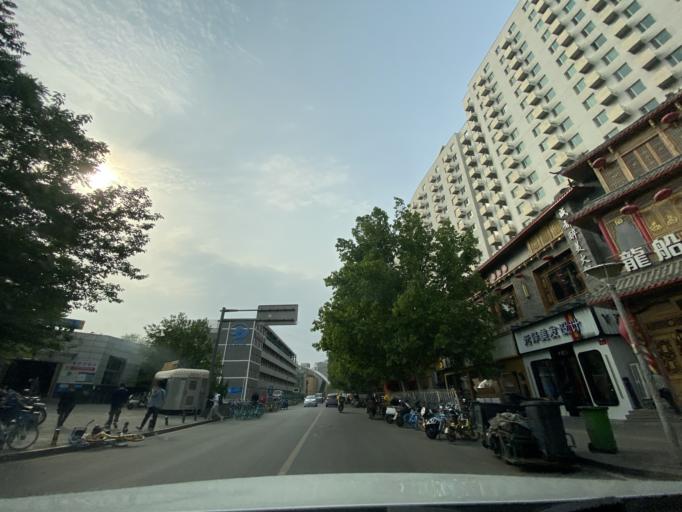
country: CN
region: Beijing
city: Haidian
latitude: 39.9754
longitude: 116.3370
